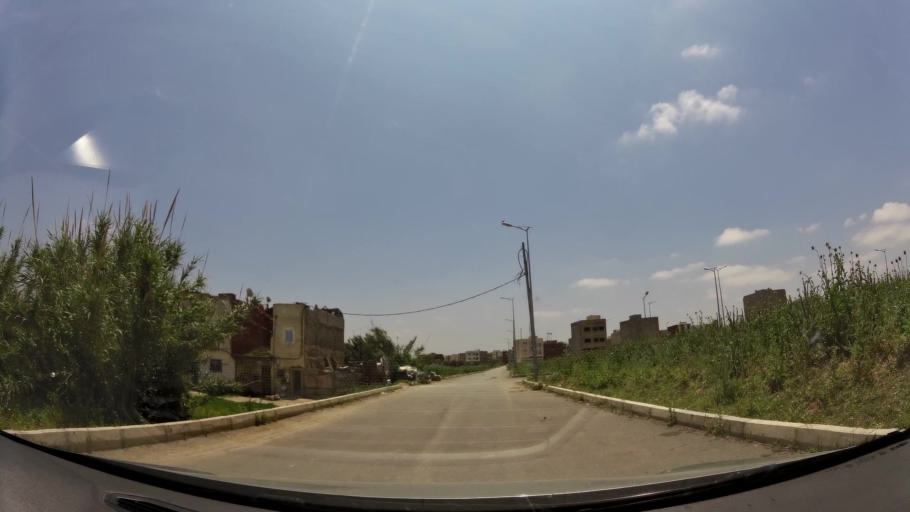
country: MA
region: Fes-Boulemane
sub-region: Fes
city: Fes
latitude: 34.0384
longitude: -5.0540
